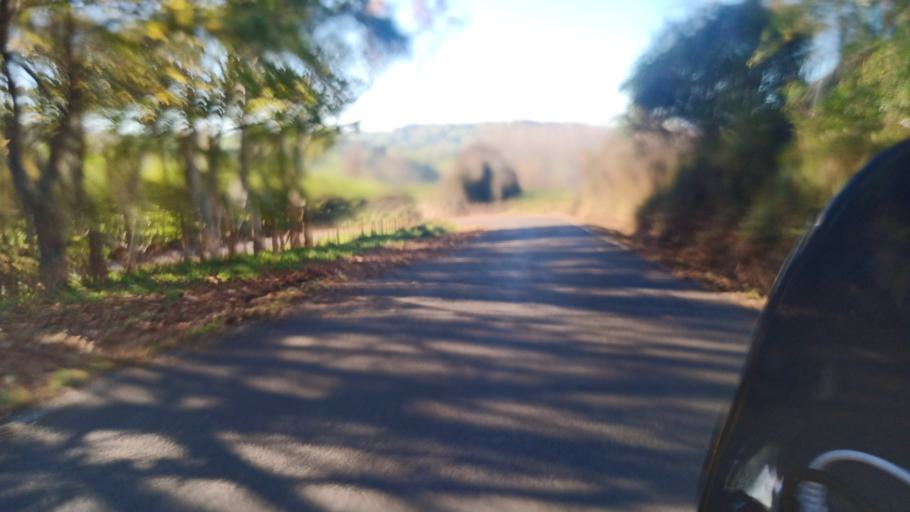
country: NZ
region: Hawke's Bay
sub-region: Wairoa District
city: Wairoa
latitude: -38.8217
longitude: 177.2920
